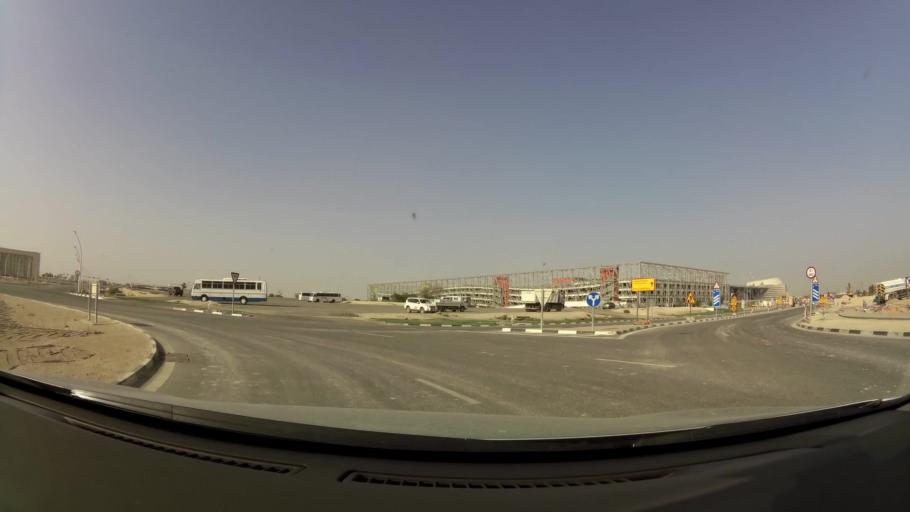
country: QA
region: Baladiyat ar Rayyan
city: Ar Rayyan
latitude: 25.3190
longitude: 51.4311
